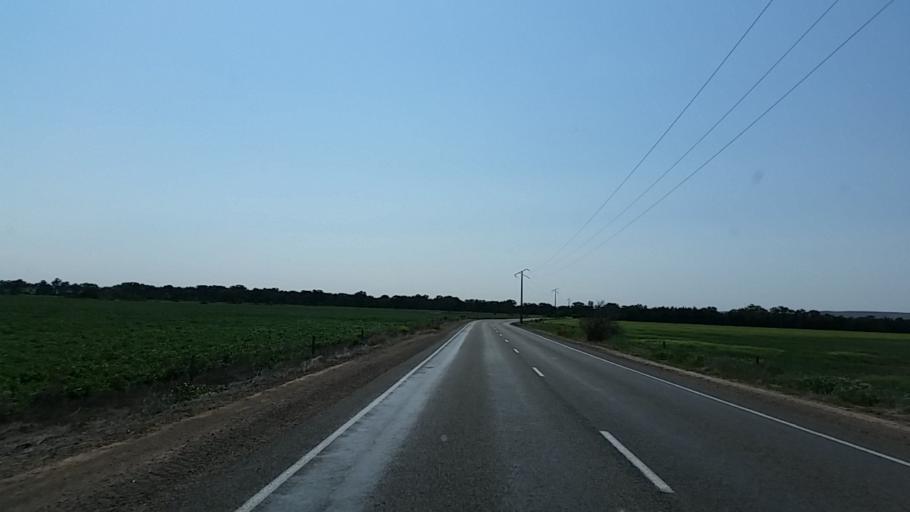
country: AU
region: South Australia
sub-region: Port Pirie City and Dists
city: Crystal Brook
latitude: -33.2677
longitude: 138.3237
